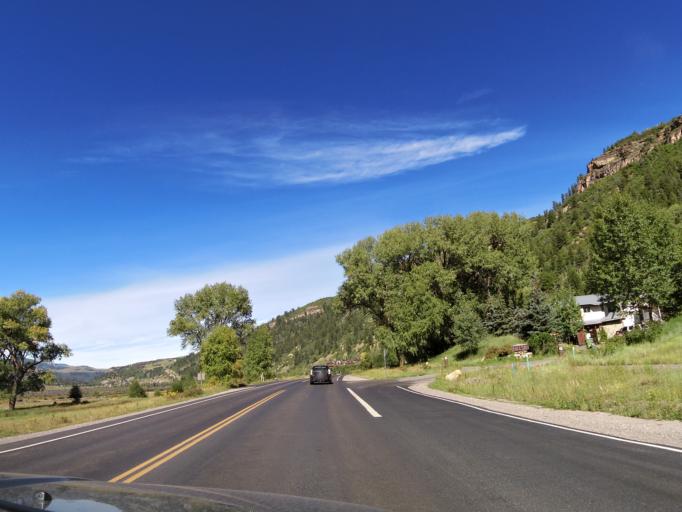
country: US
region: Colorado
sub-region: San Miguel County
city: Mountain Village
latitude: 37.9486
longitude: -107.8485
